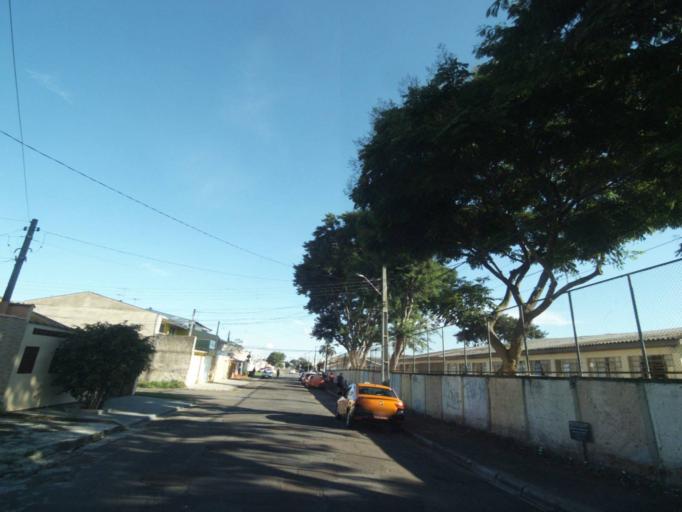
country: BR
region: Parana
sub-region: Pinhais
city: Pinhais
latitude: -25.4574
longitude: -49.2042
